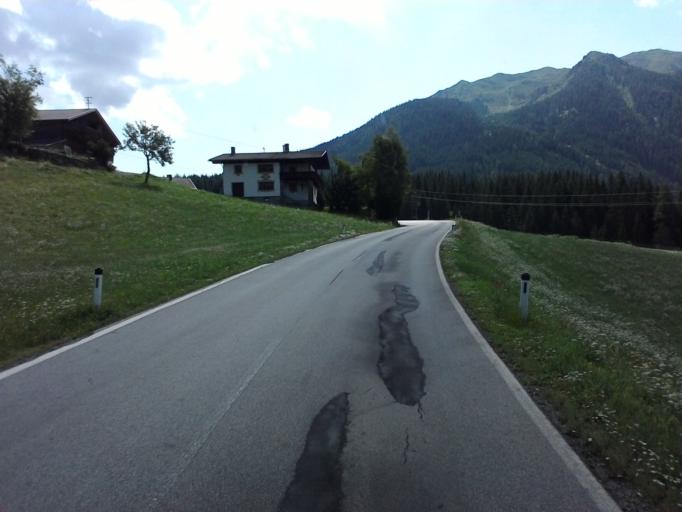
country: AT
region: Tyrol
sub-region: Politischer Bezirk Lienz
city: Kartitsch
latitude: 46.7206
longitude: 12.5205
